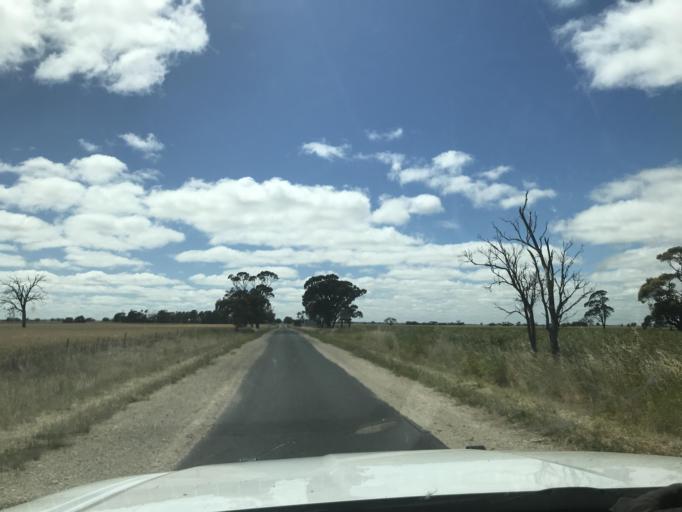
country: AU
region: South Australia
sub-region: Tatiara
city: Bordertown
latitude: -36.2800
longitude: 141.1301
